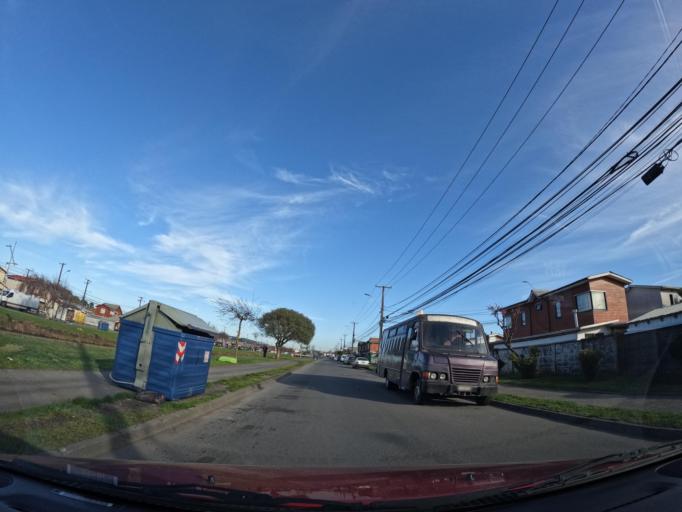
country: CL
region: Biobio
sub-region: Provincia de Concepcion
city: Talcahuano
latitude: -36.7568
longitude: -73.0849
